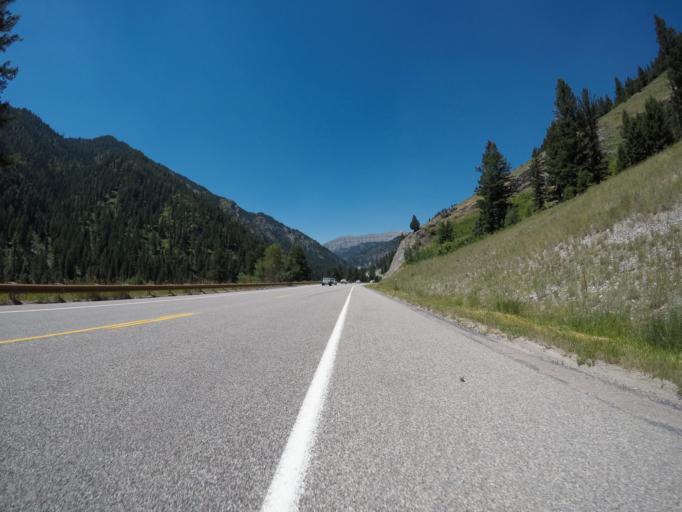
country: US
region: Wyoming
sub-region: Teton County
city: Hoback
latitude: 43.1960
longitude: -110.8768
